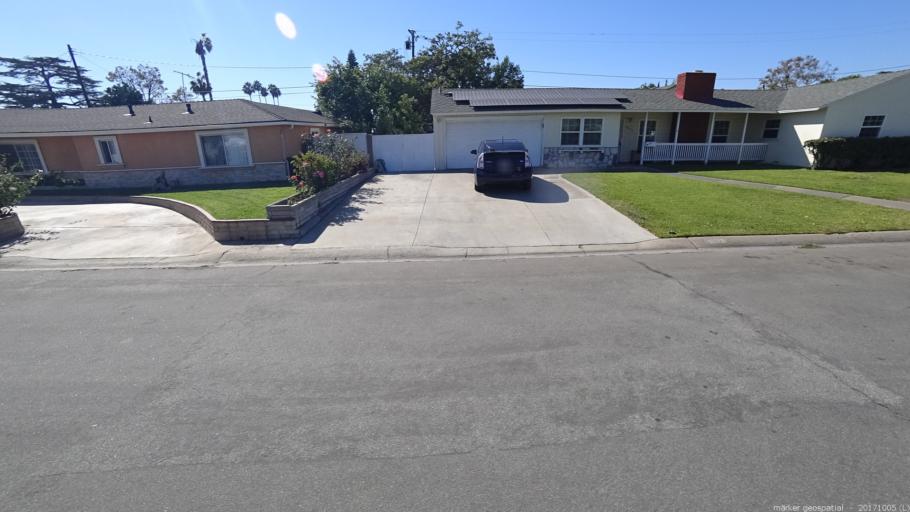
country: US
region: California
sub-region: Orange County
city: Garden Grove
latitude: 33.7859
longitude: -117.9554
